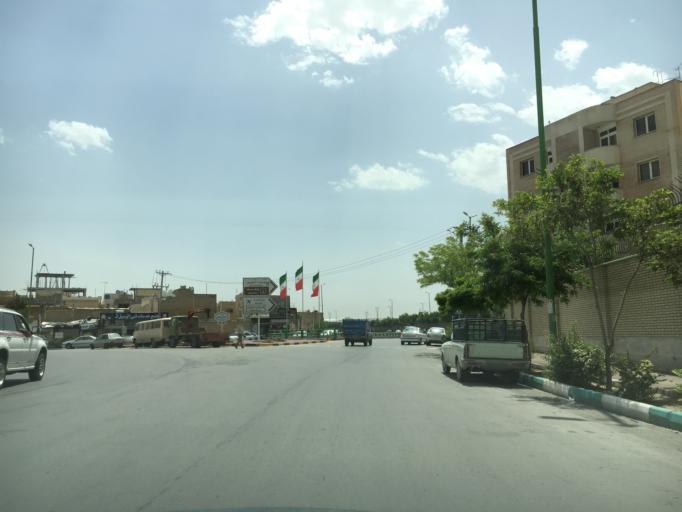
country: IR
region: Isfahan
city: Isfahan
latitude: 32.6246
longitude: 51.6911
